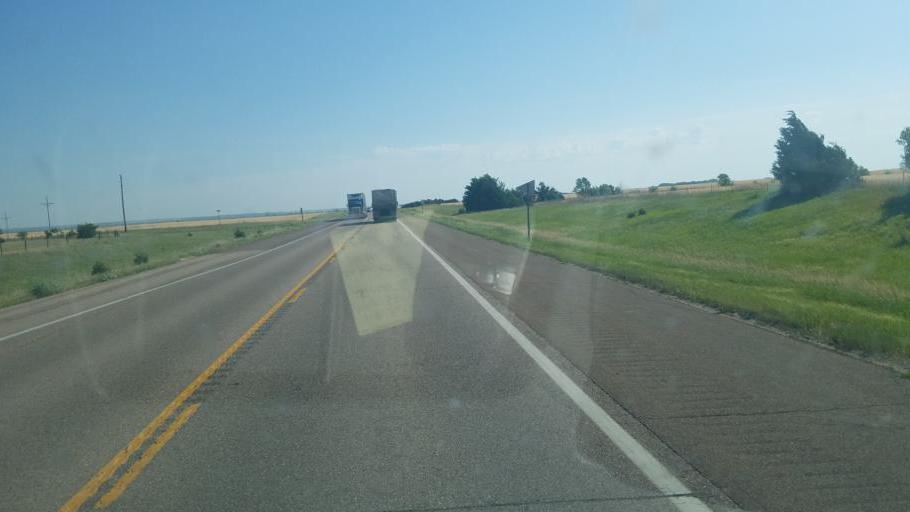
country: US
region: Kansas
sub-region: Barton County
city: Ellinwood
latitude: 38.4065
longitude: -98.6642
